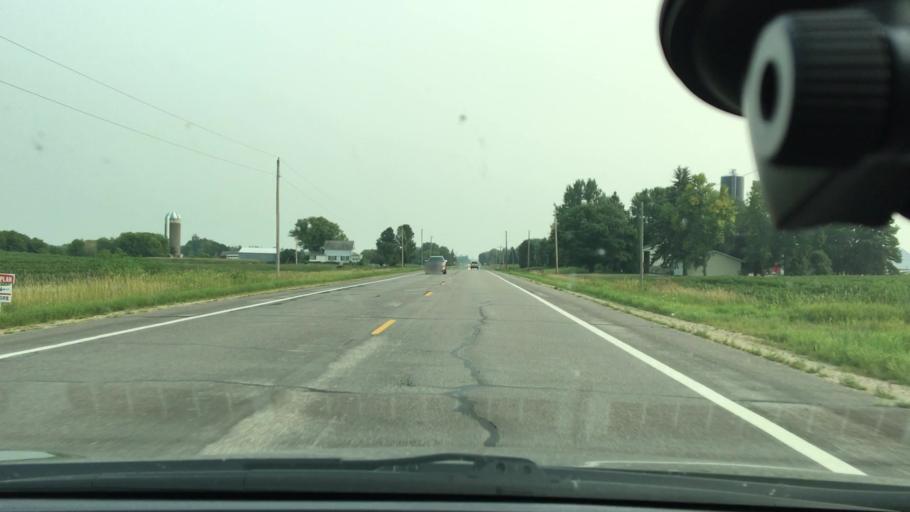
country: US
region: Minnesota
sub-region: Wright County
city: Albertville
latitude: 45.2729
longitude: -93.6637
